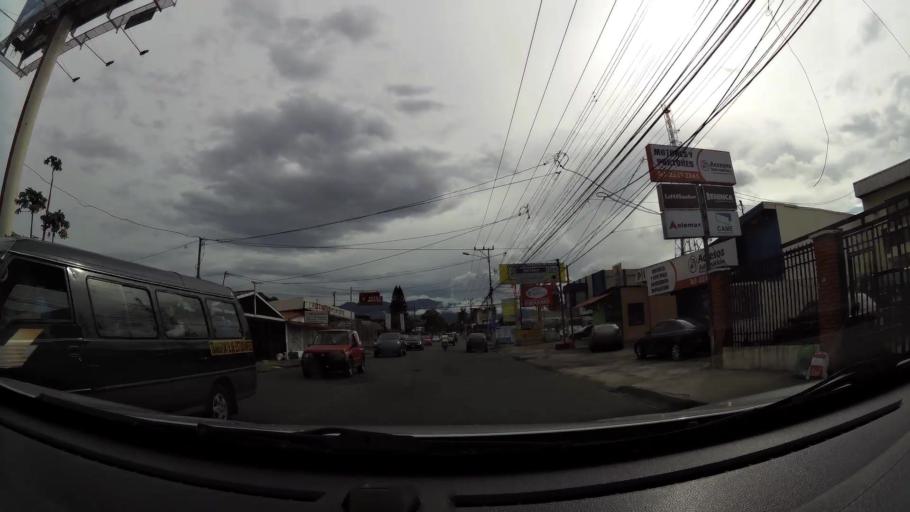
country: CR
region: San Jose
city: Calle Blancos
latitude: 9.9620
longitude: -84.0682
